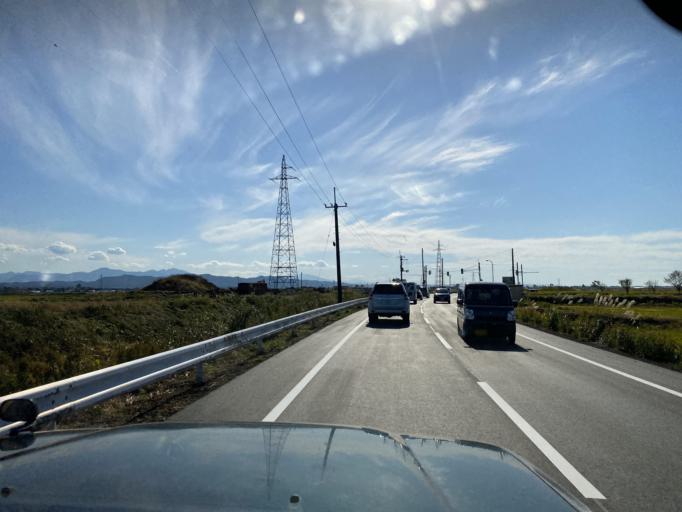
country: JP
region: Niigata
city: Niitsu-honcho
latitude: 37.8070
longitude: 139.0794
